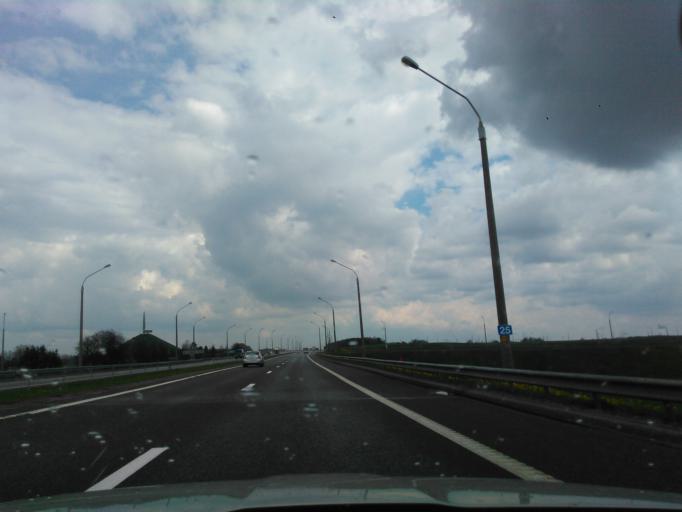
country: BY
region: Minsk
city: Slabada
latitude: 54.0149
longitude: 27.8857
